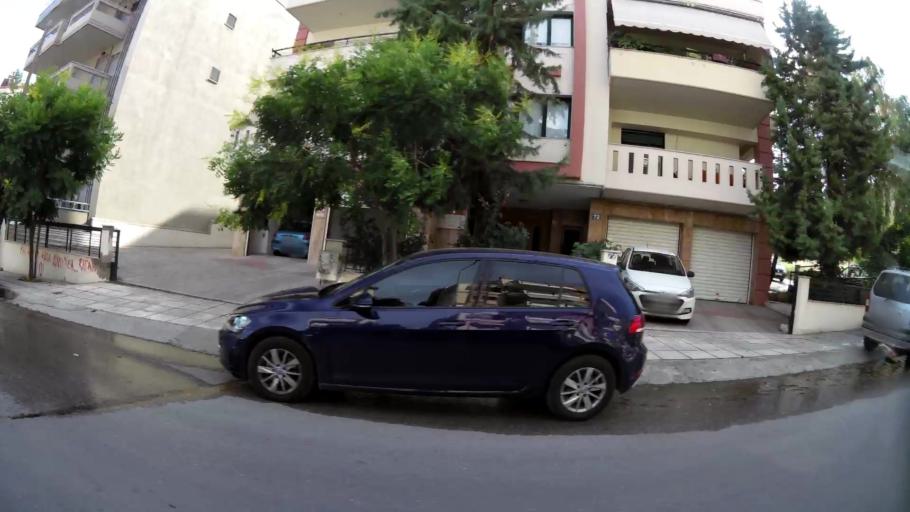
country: GR
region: Central Macedonia
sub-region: Nomos Thessalonikis
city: Kalamaria
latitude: 40.5731
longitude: 22.9690
